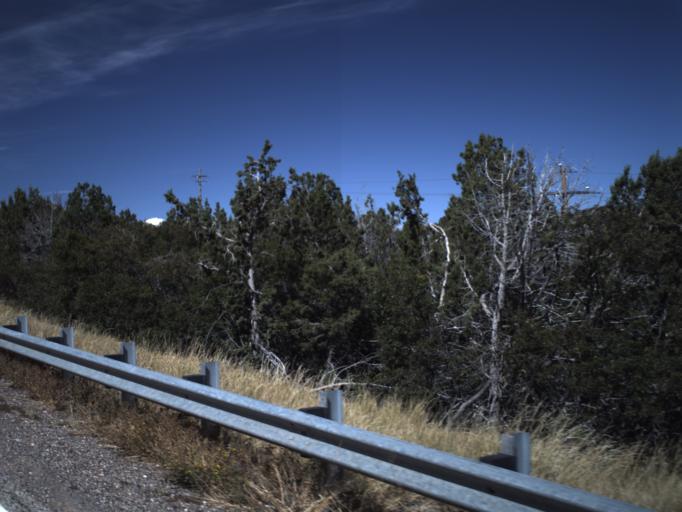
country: US
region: Utah
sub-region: Washington County
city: Enterprise
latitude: 37.5202
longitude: -113.6381
